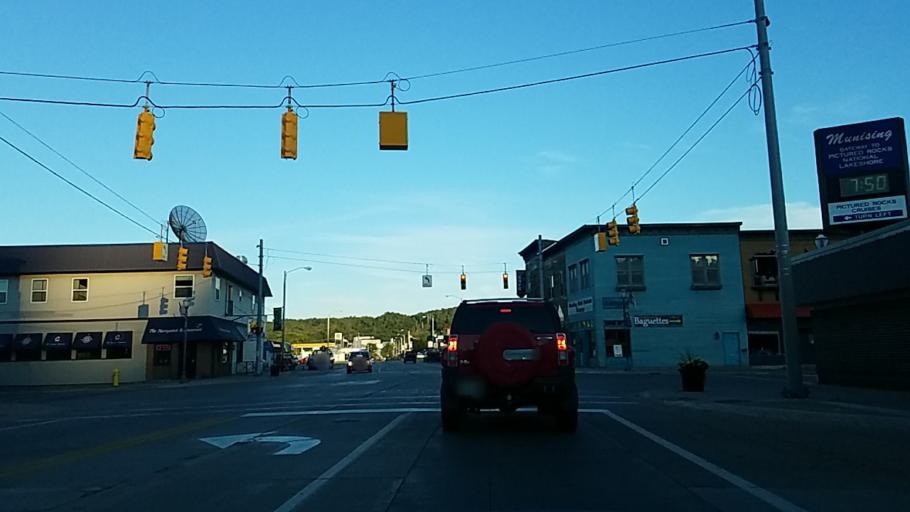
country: US
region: Michigan
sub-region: Alger County
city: Munising
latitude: 46.4117
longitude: -86.6554
